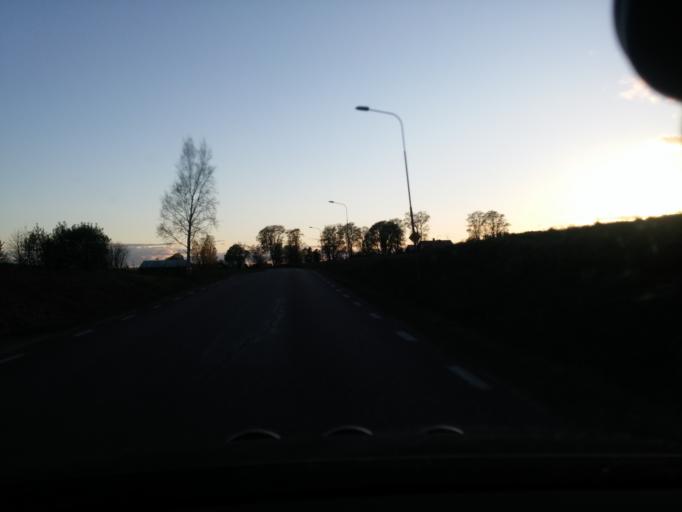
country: SE
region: Gaevleborg
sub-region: Bollnas Kommun
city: Bollnas
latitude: 61.4067
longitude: 16.5546
